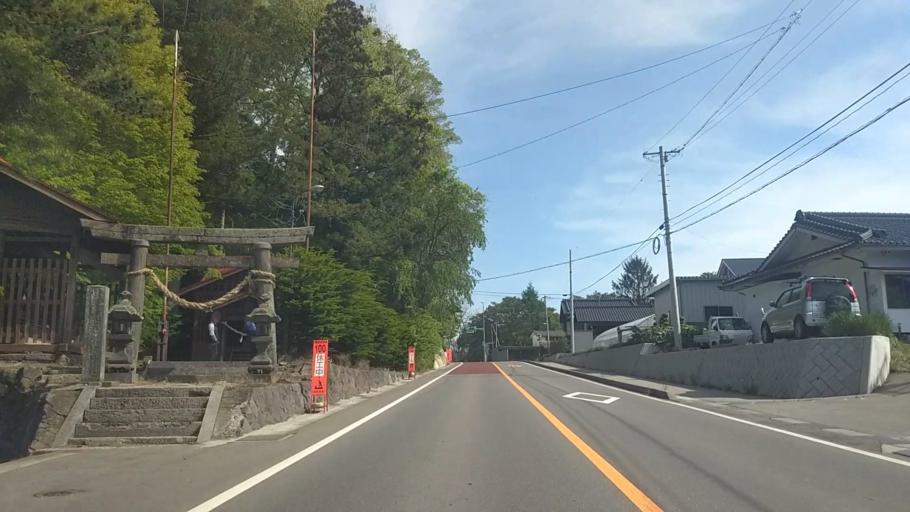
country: JP
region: Nagano
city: Saku
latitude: 36.0404
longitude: 138.4715
